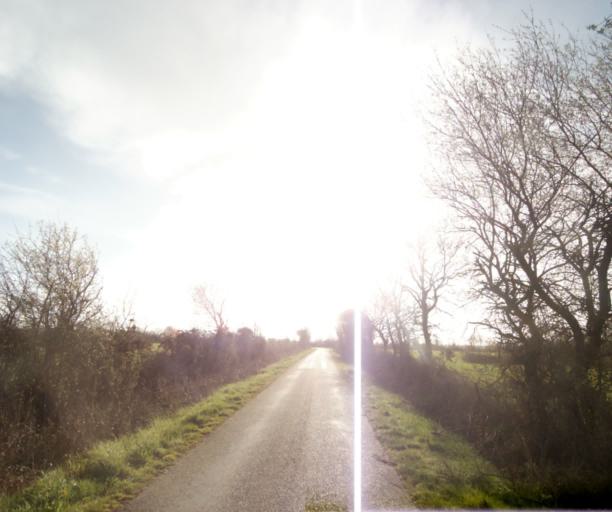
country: FR
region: Pays de la Loire
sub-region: Departement de la Loire-Atlantique
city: Malville
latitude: 47.3949
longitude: -1.8972
